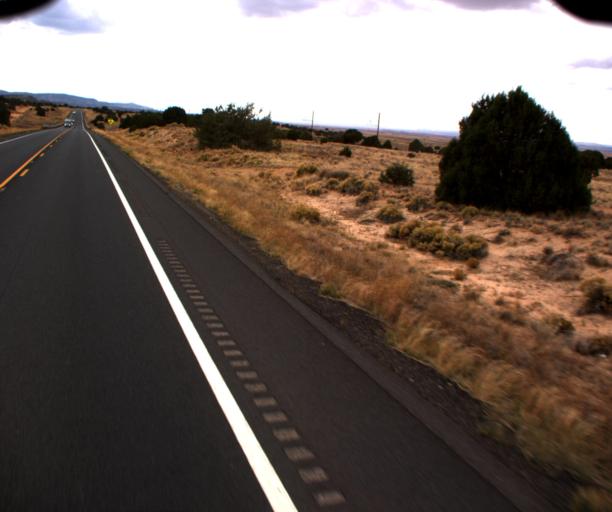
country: US
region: Arizona
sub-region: Navajo County
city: Kayenta
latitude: 36.4968
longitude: -110.6234
